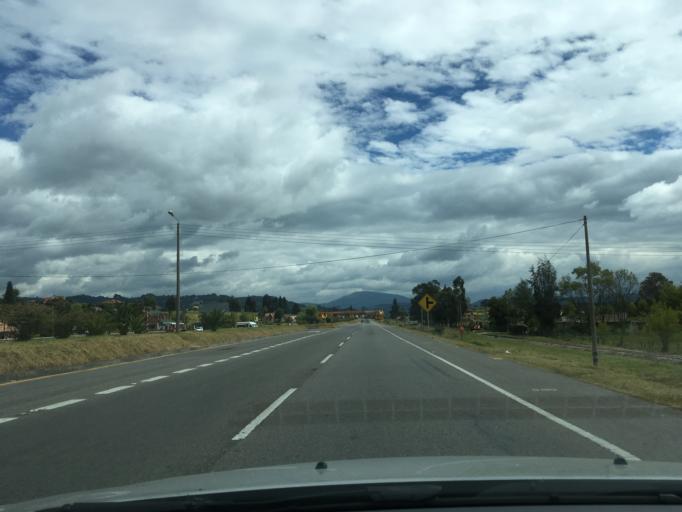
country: CO
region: Boyaca
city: Paipa
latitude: 5.7851
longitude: -73.0910
